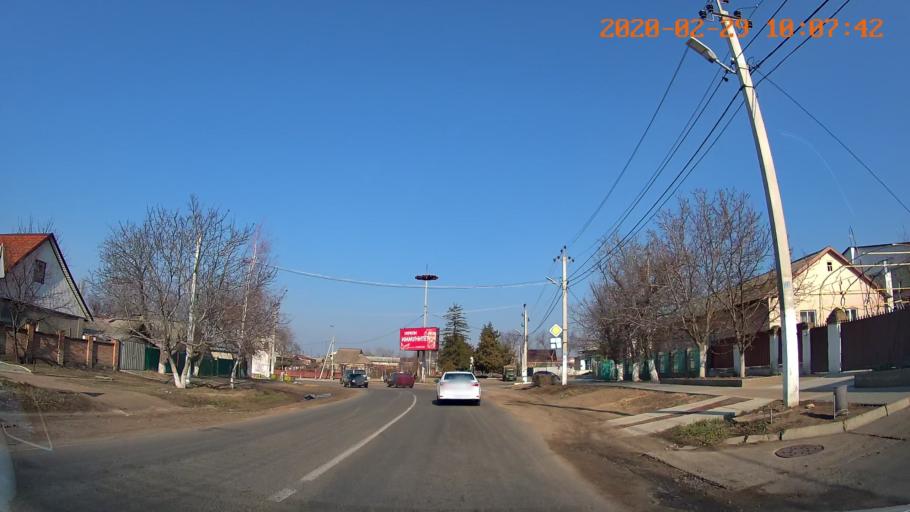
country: MD
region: Telenesti
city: Tiraspolul Nou
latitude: 46.8226
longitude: 29.6639
